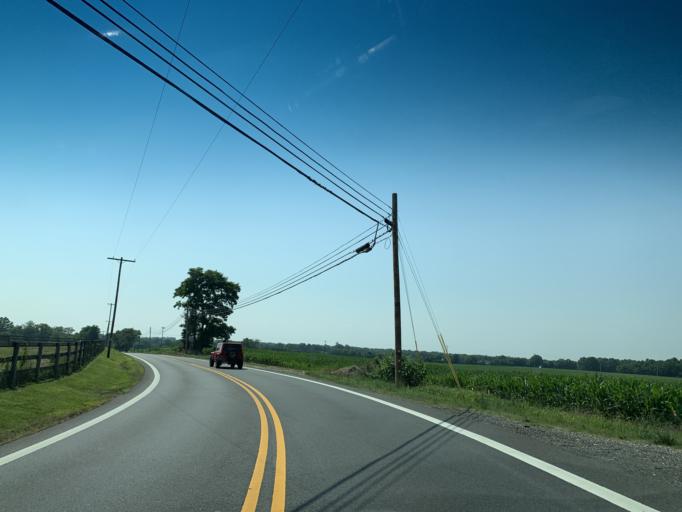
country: US
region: Maryland
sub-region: Montgomery County
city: Poolesville
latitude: 39.1324
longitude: -77.3856
